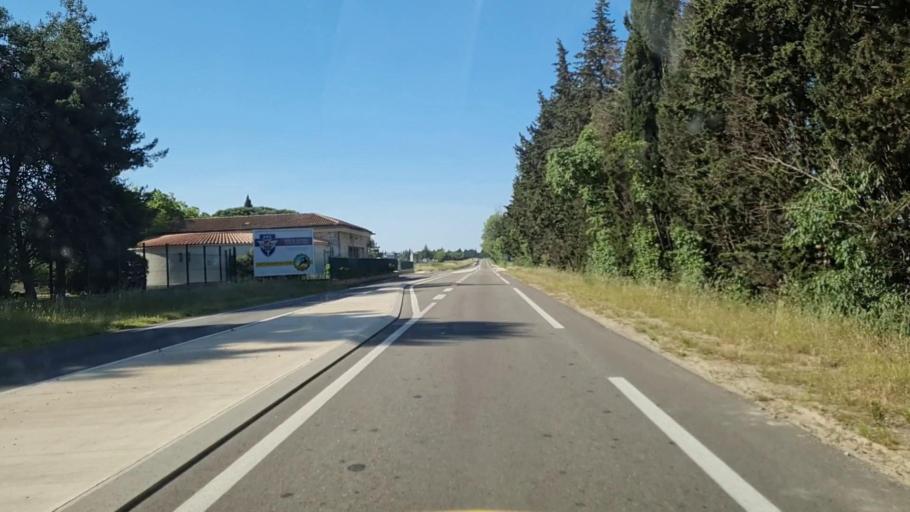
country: FR
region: Languedoc-Roussillon
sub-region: Departement du Gard
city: Garons
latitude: 43.7612
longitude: 4.4058
